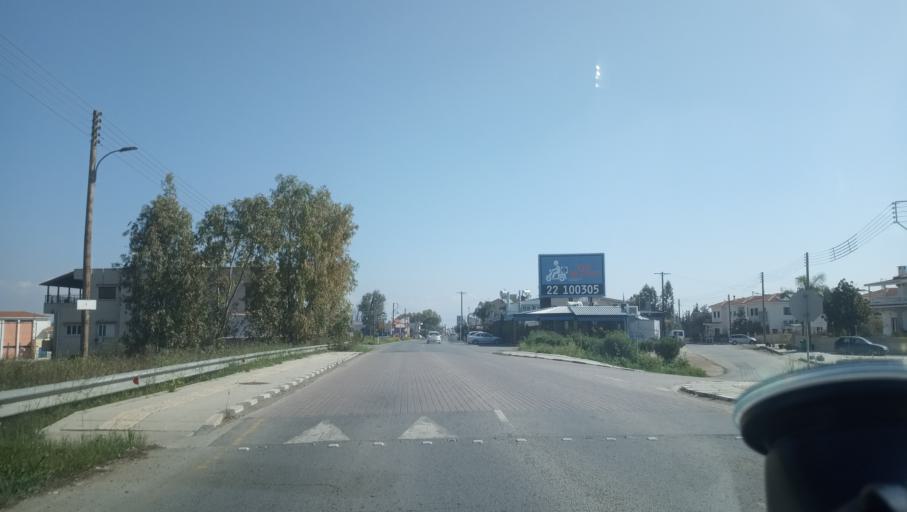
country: CY
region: Lefkosia
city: Kato Deftera
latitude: 35.0959
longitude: 33.2943
